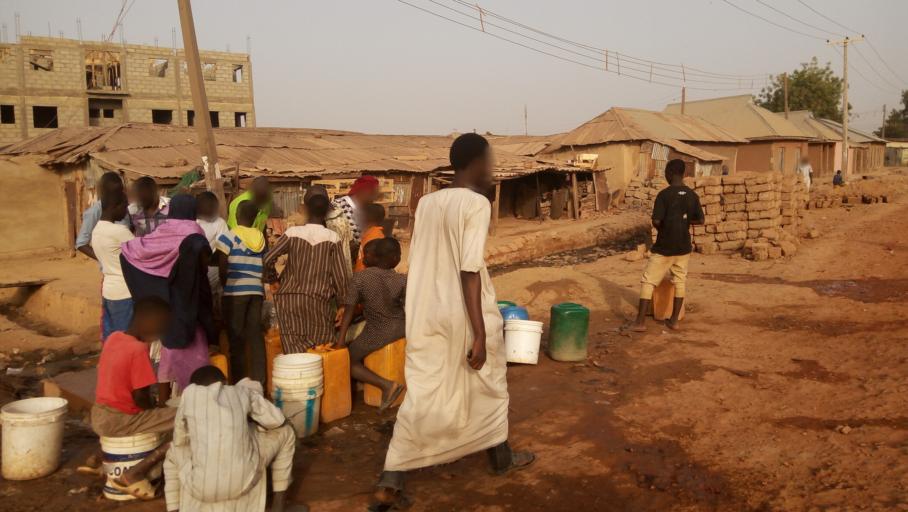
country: NG
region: Kaduna
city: Zaria
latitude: 11.1629
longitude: 7.6537
